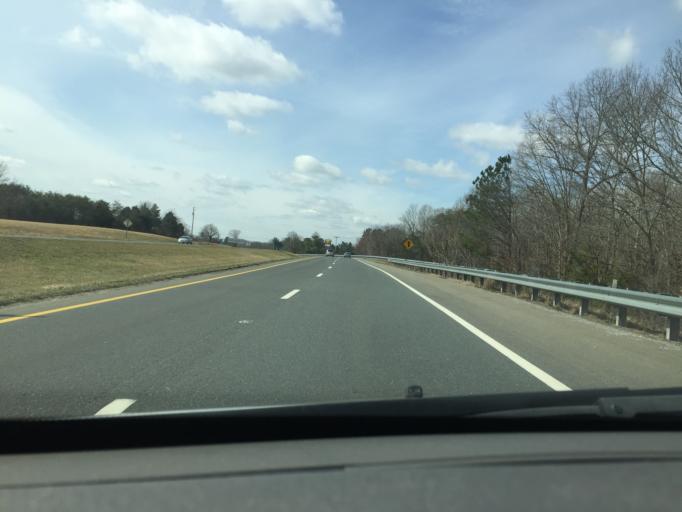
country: US
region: Virginia
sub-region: Campbell County
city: Timberlake
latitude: 37.3103
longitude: -79.2637
